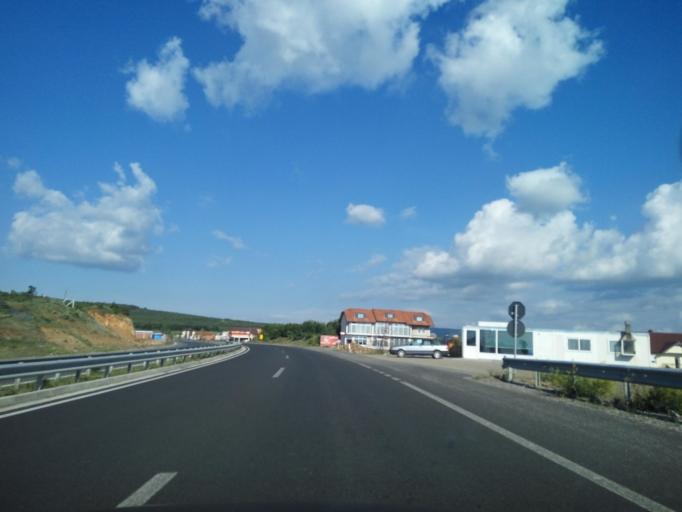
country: XK
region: Prizren
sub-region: Komuna e Malisheves
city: Llazice
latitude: 42.5648
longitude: 20.7650
